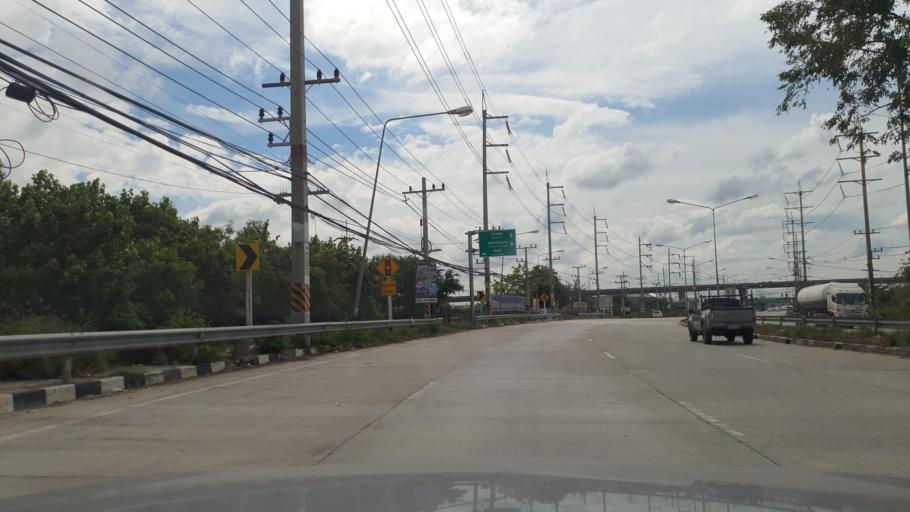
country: TH
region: Chachoengsao
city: Bang Pakong
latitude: 13.5151
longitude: 100.9900
